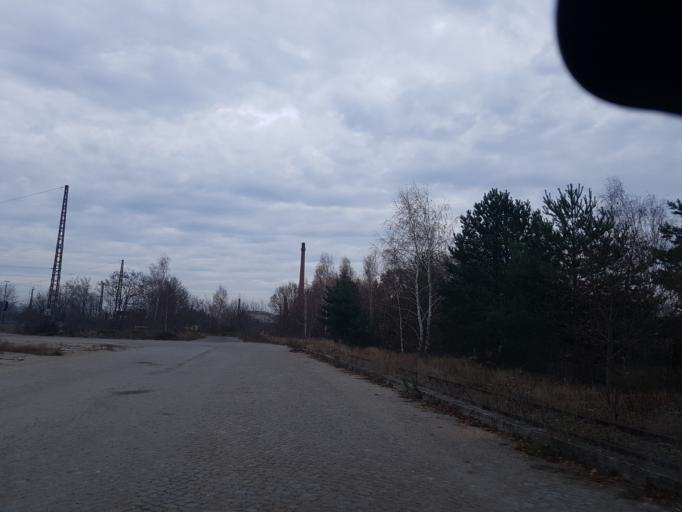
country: DE
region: Brandenburg
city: Finsterwalde
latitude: 51.6390
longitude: 13.7168
